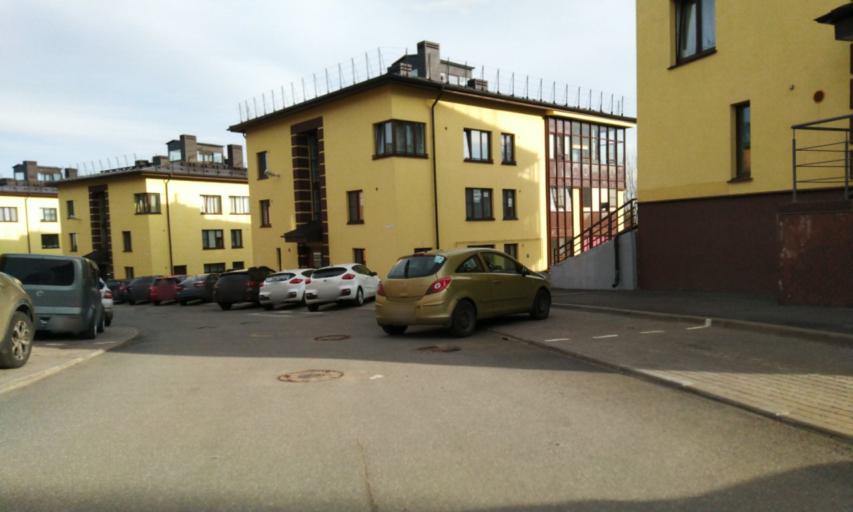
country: RU
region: Leningrad
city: Bugry
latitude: 60.1190
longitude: 30.4245
